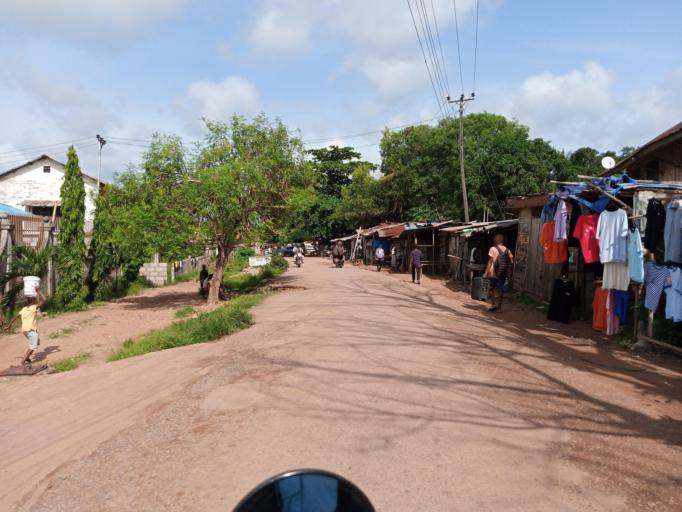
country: SL
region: Southern Province
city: Bo
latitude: 7.9604
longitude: -11.7427
